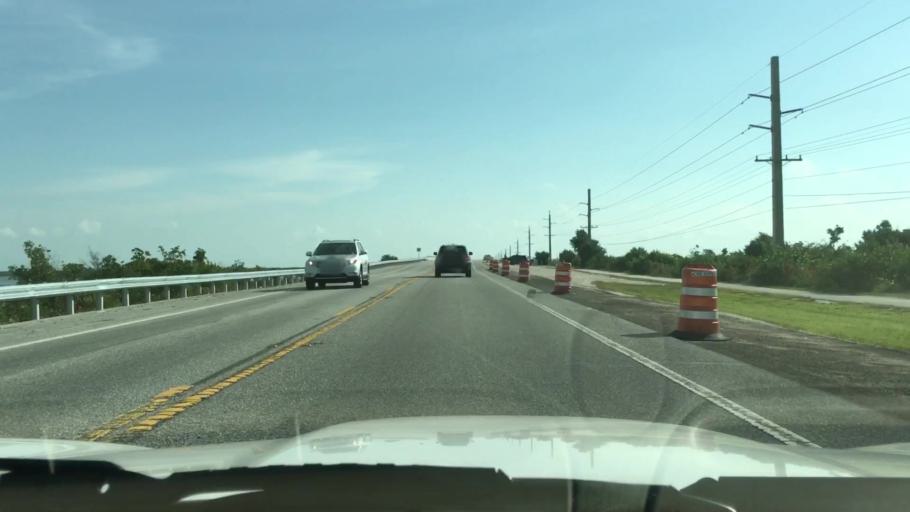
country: US
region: Florida
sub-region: Monroe County
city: Cudjoe Key
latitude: 24.6629
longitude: -81.4693
